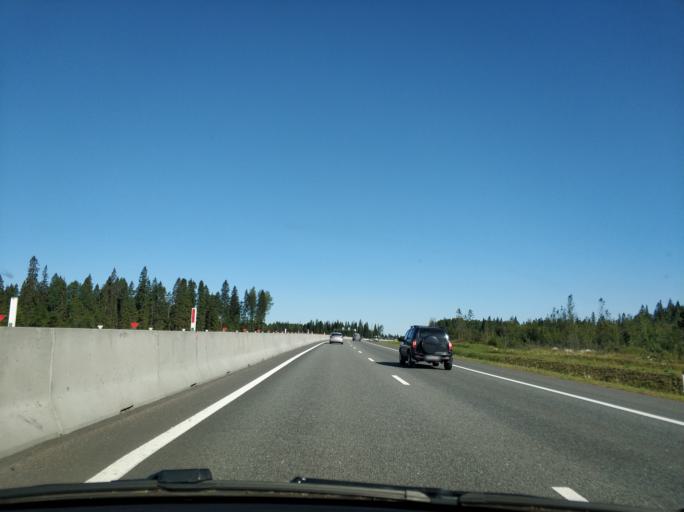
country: RU
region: Leningrad
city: Sosnovo
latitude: 60.4426
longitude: 30.2097
